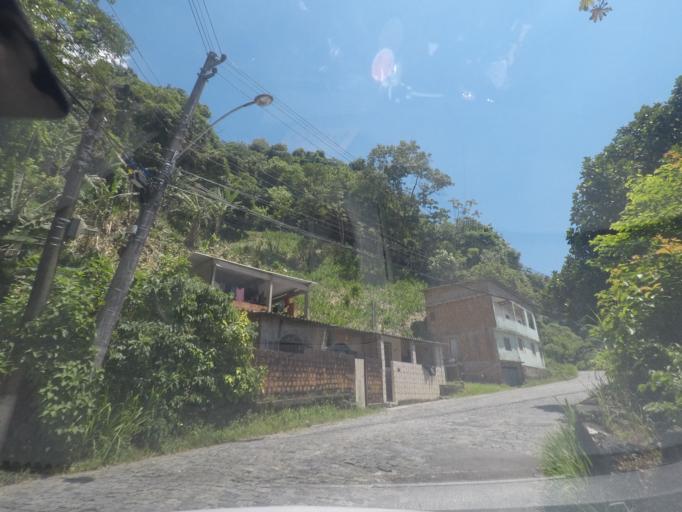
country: BR
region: Rio de Janeiro
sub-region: Petropolis
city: Petropolis
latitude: -22.5355
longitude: -43.1749
